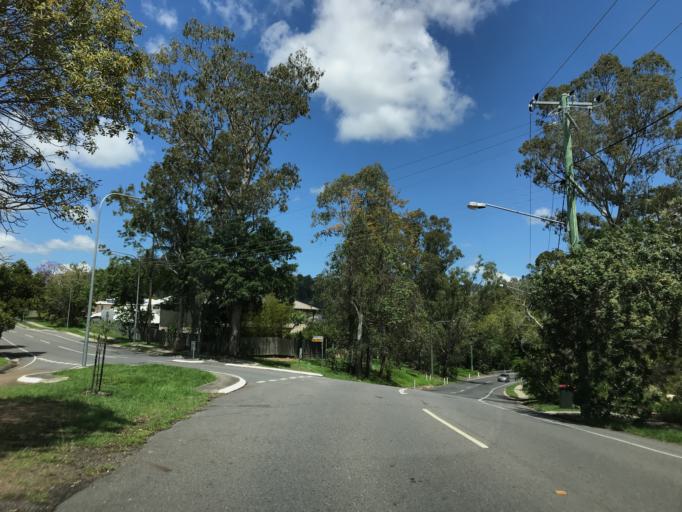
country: AU
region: Queensland
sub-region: Brisbane
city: Kenmore Hills
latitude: -27.4515
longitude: 152.9400
